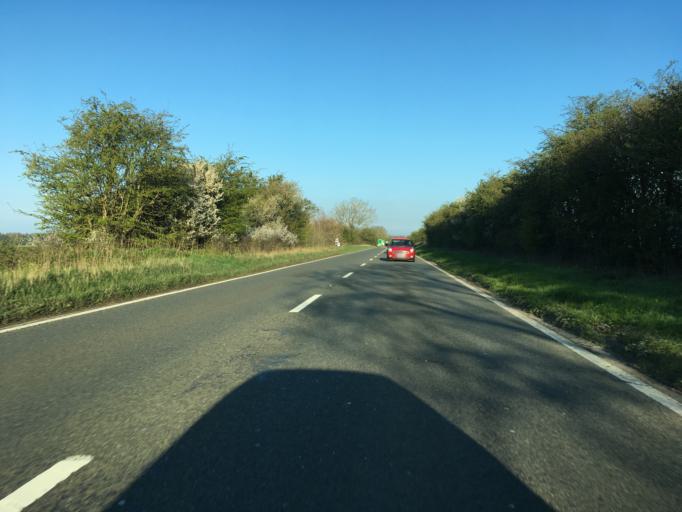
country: GB
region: England
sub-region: Oxfordshire
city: Burford
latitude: 51.8066
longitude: -1.6549
